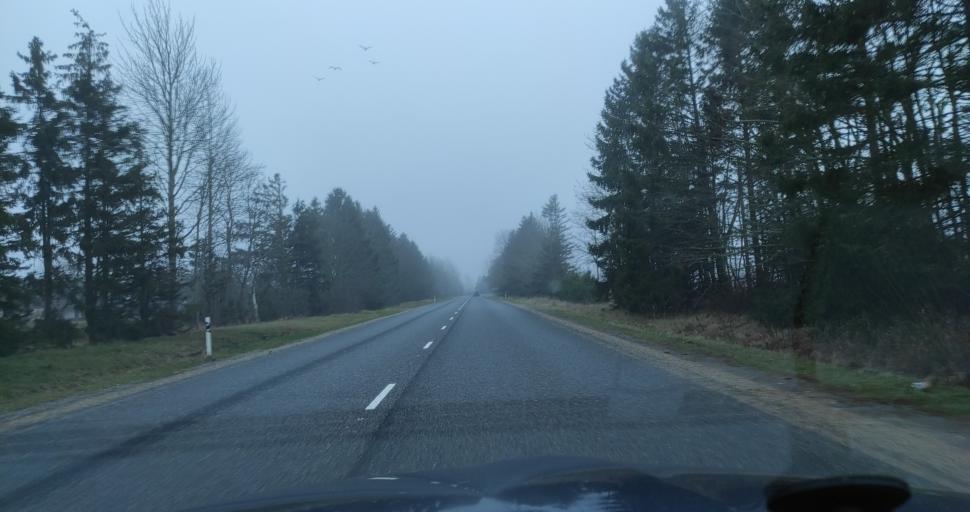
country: LV
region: Alsunga
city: Alsunga
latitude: 57.0043
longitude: 21.3858
